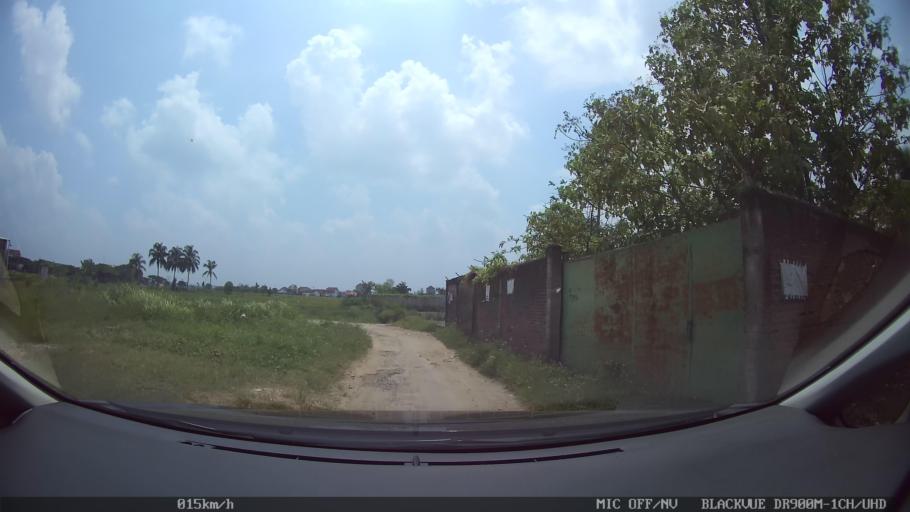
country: ID
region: Lampung
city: Pringsewu
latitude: -5.3559
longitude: 104.9893
